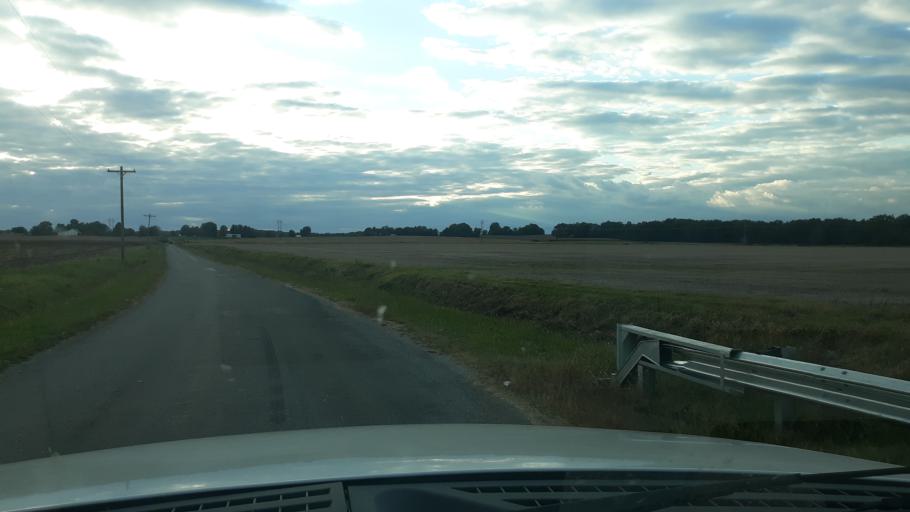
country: US
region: Illinois
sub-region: Saline County
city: Eldorado
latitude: 37.8378
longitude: -88.4528
